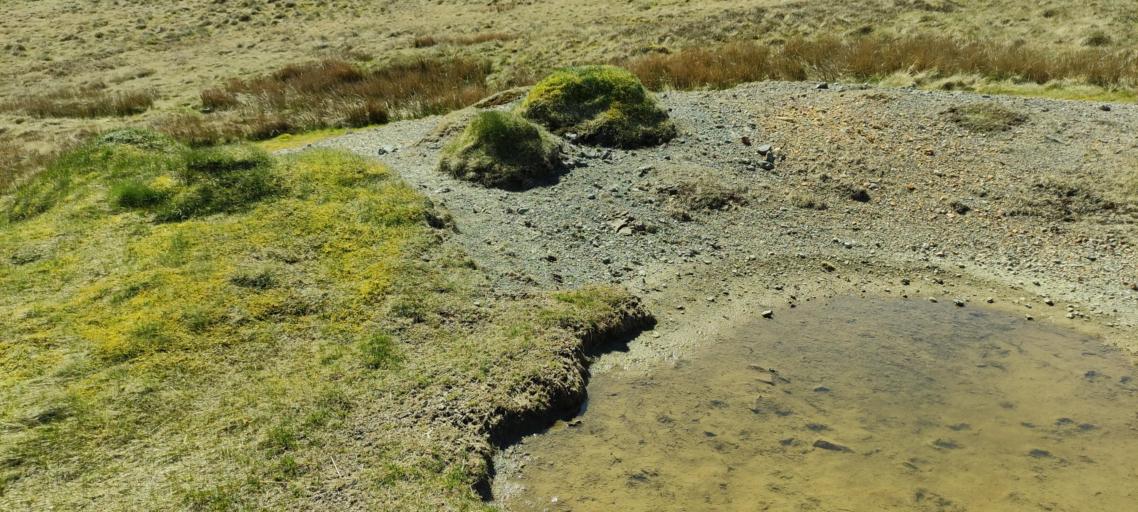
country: GB
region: England
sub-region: Cumbria
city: Keswick
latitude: 54.6960
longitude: -3.0911
